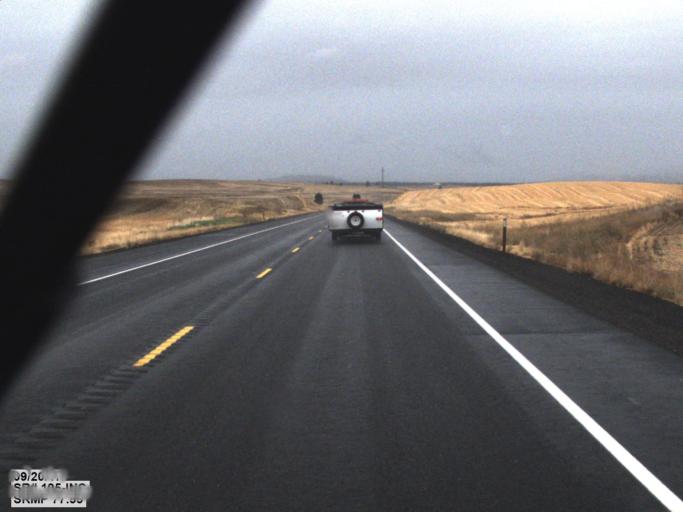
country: US
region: Washington
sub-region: Spokane County
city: Cheney
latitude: 47.4051
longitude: -117.3916
